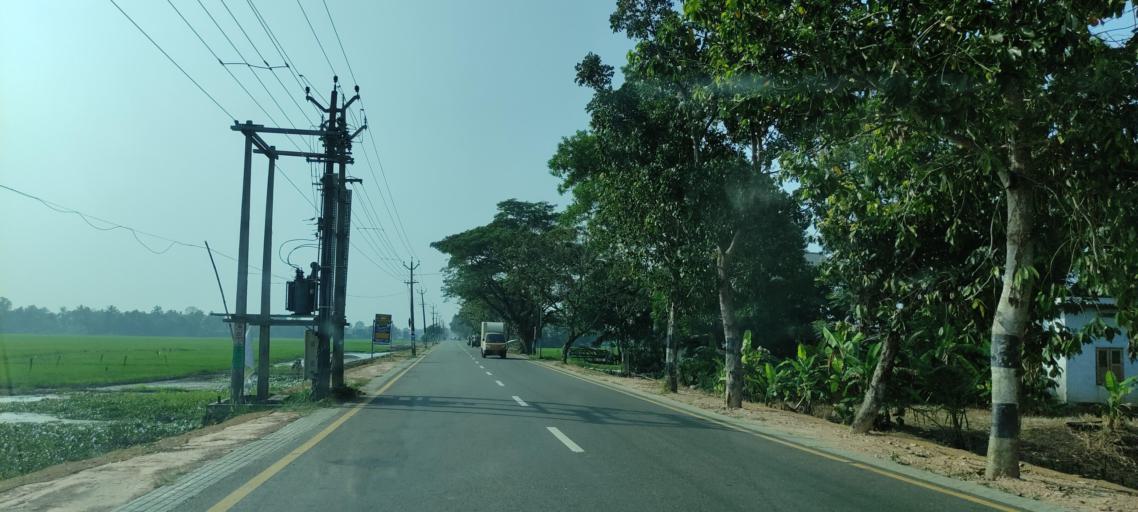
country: IN
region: Kerala
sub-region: Kottayam
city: Changanacheri
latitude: 9.3649
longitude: 76.4411
